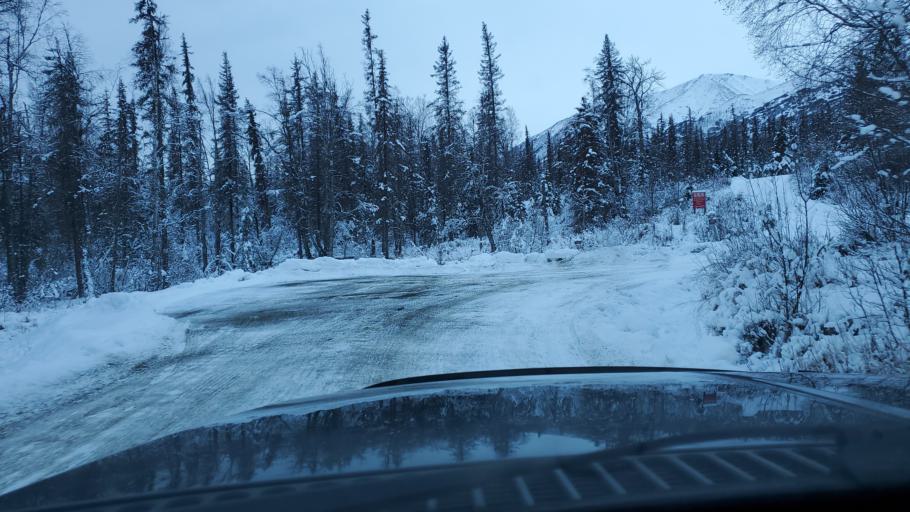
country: US
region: Alaska
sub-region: Matanuska-Susitna Borough
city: Lakes
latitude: 61.6969
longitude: -149.3254
